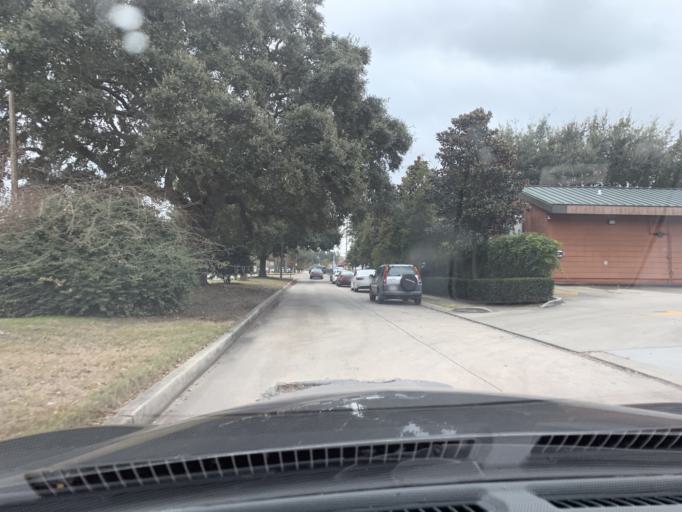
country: US
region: Louisiana
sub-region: Jefferson Parish
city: Metairie
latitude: 30.0051
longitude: -90.1027
